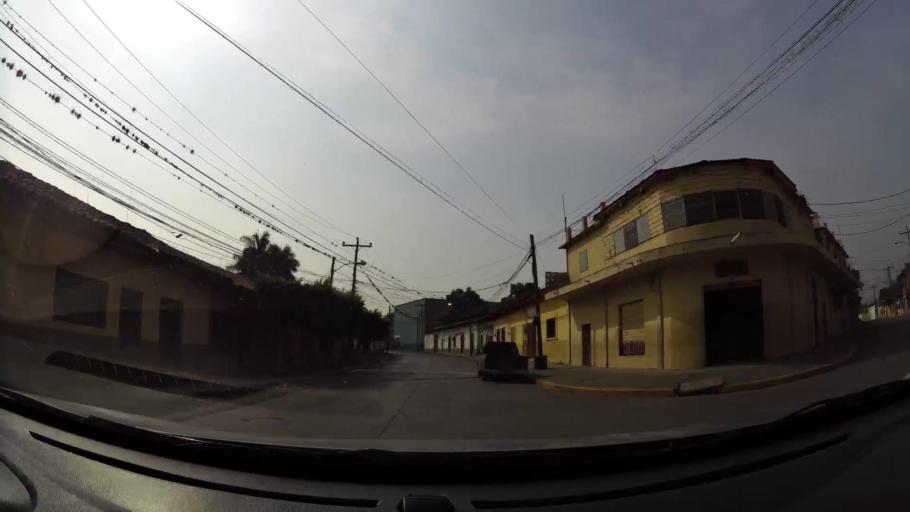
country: HN
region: Comayagua
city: Comayagua
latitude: 14.4629
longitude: -87.6438
